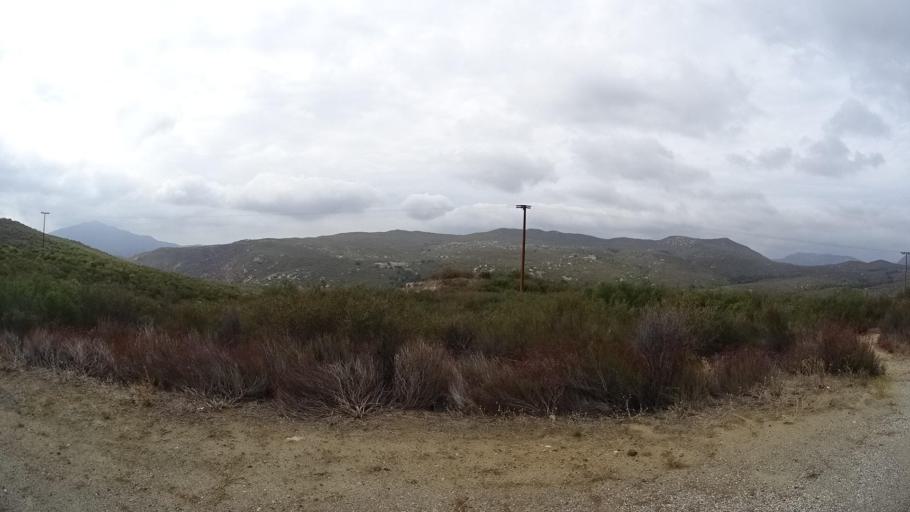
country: US
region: California
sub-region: San Diego County
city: Descanso
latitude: 32.8943
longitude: -116.6487
